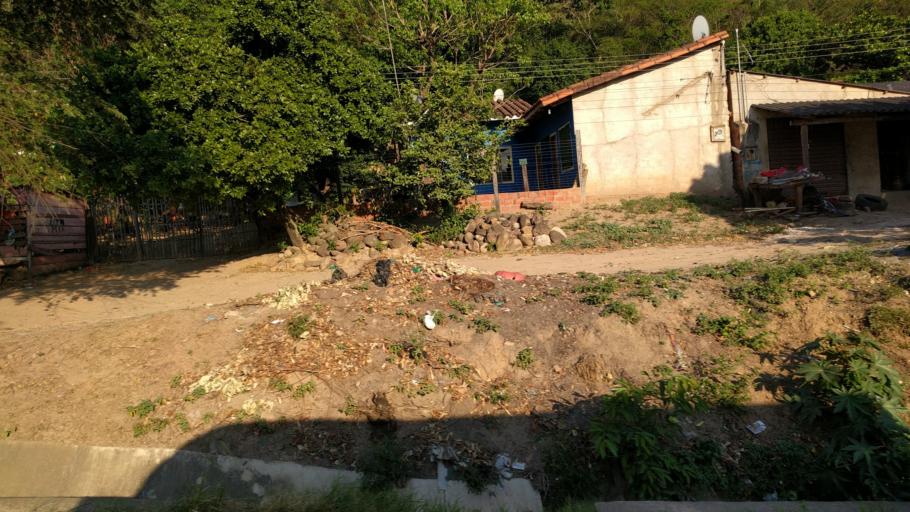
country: BO
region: Santa Cruz
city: Limoncito
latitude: -18.0249
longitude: -63.4006
